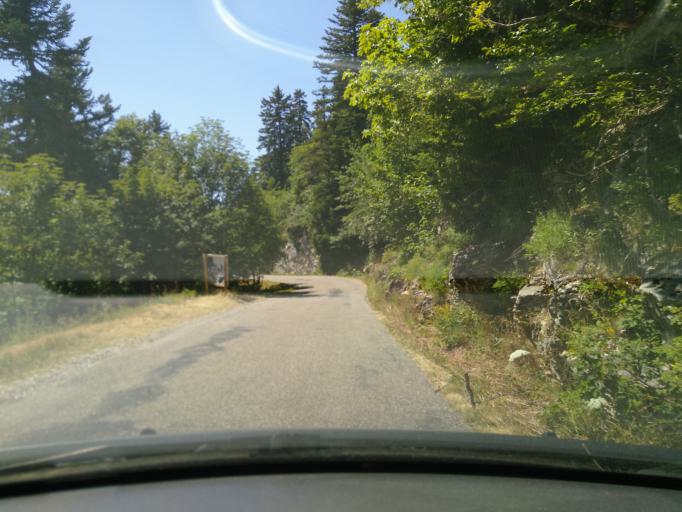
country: FR
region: Rhone-Alpes
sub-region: Departement de l'Isere
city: Le Sappey-en-Chartreuse
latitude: 45.3092
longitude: 5.7536
